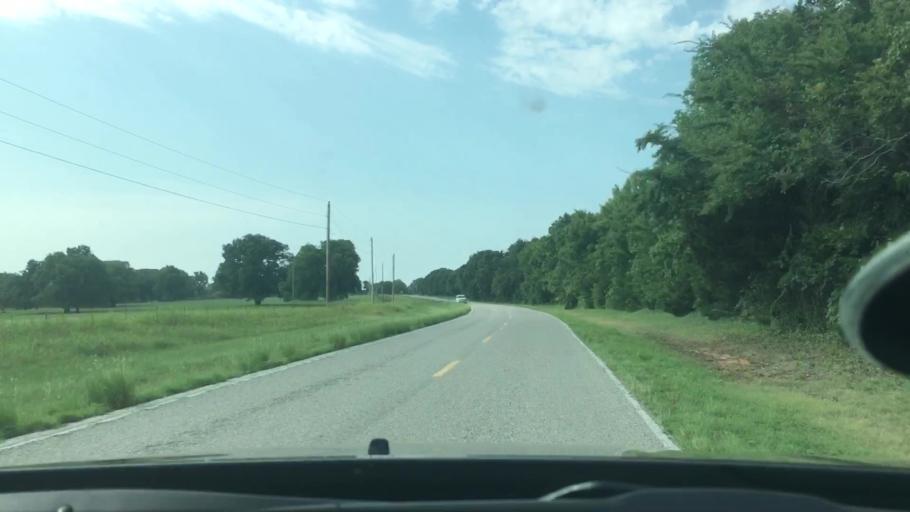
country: US
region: Oklahoma
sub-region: Johnston County
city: Tishomingo
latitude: 34.1911
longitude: -96.5790
